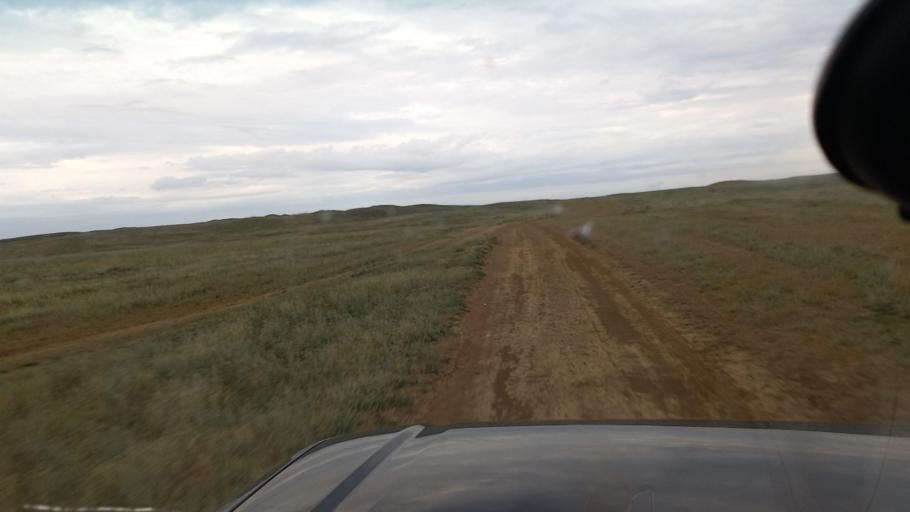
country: RU
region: Krasnodarskiy
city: Taman'
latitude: 45.2018
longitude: 36.7802
